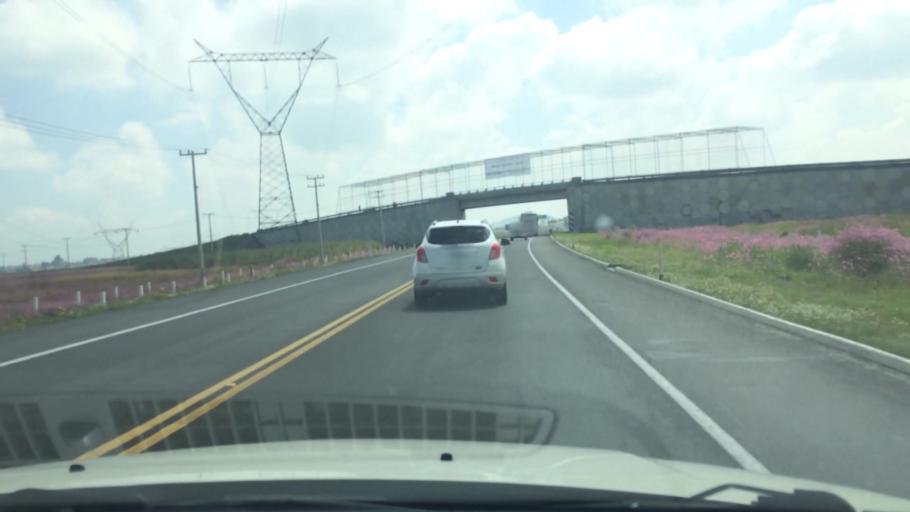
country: MX
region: Mexico
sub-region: Toluca
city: Sebastian Lerdo de Tejada
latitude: 19.3883
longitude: -99.7221
